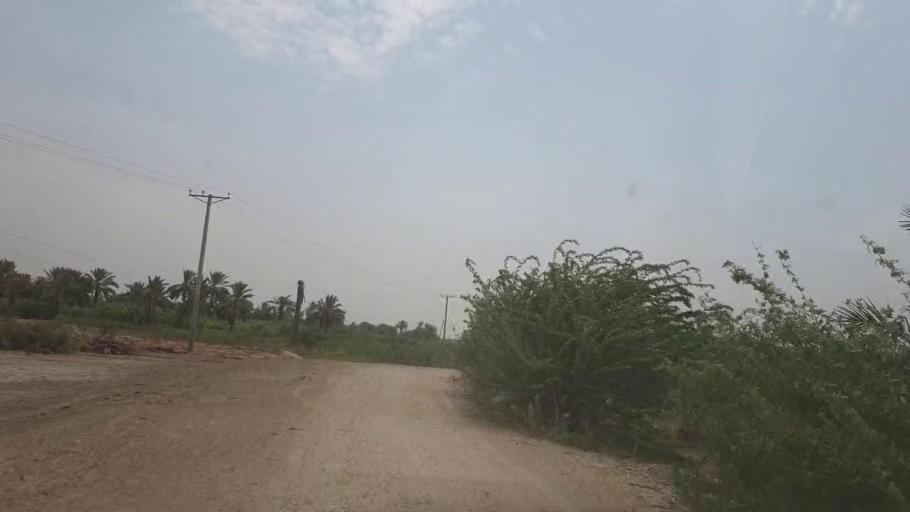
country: PK
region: Sindh
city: Kot Diji
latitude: 27.4247
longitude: 68.6986
